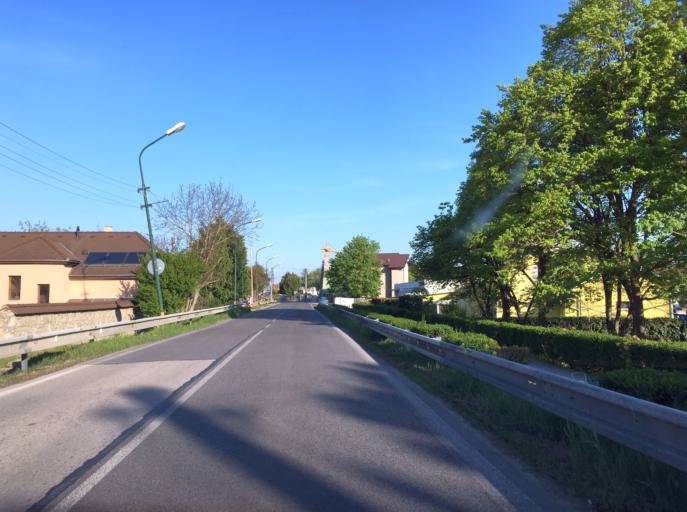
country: AT
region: Burgenland
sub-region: Politischer Bezirk Neusiedl am See
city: Deutsch Jahrndorf
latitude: 48.0649
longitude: 17.1140
